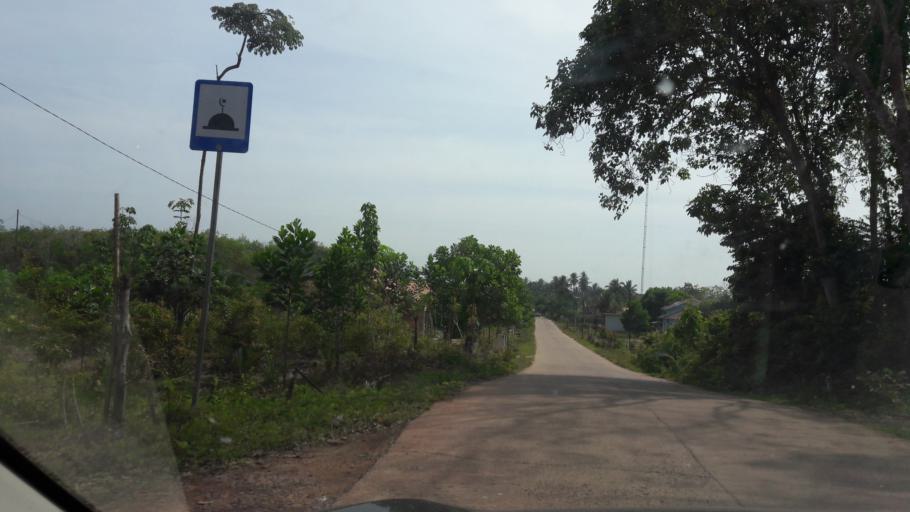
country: ID
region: South Sumatra
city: Gunungmenang
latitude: -3.3158
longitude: 104.1138
